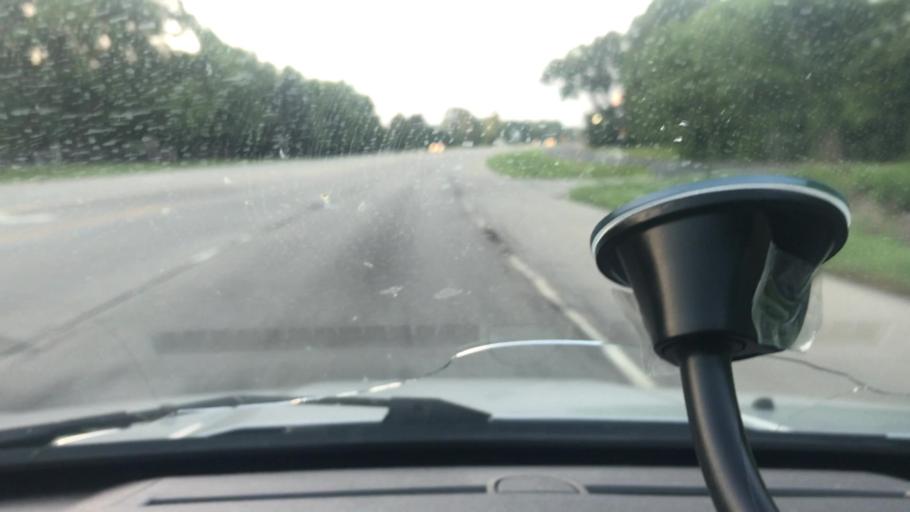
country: US
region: Illinois
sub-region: Tazewell County
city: Pekin
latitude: 40.5924
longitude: -89.6411
